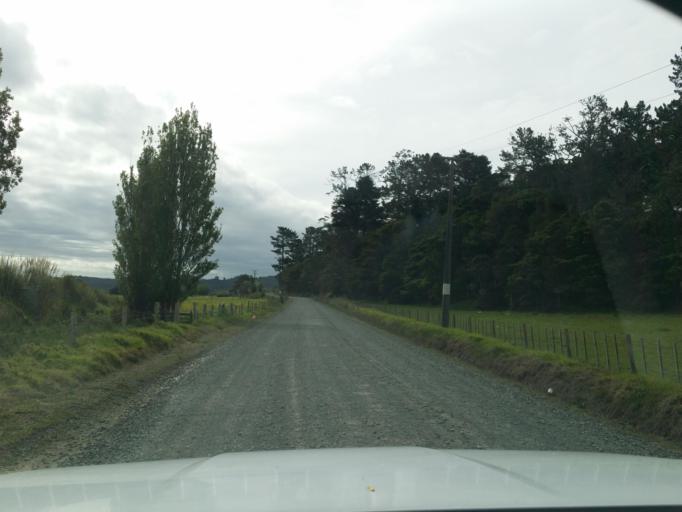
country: NZ
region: Northland
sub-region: Kaipara District
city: Dargaville
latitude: -35.8978
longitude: 173.9166
